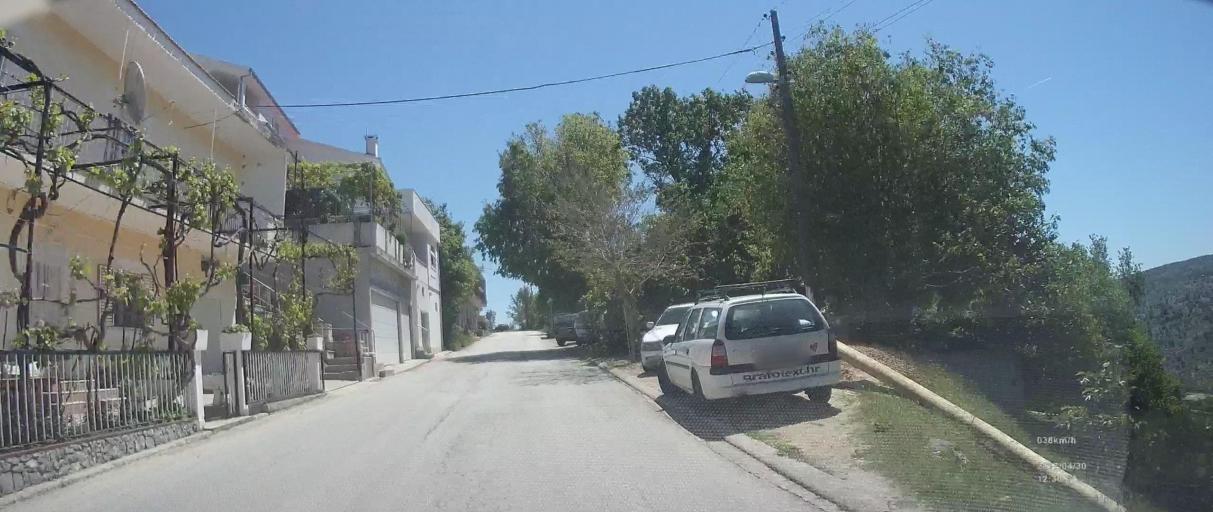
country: HR
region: Splitsko-Dalmatinska
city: Srinjine
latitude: 43.5007
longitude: 16.6042
